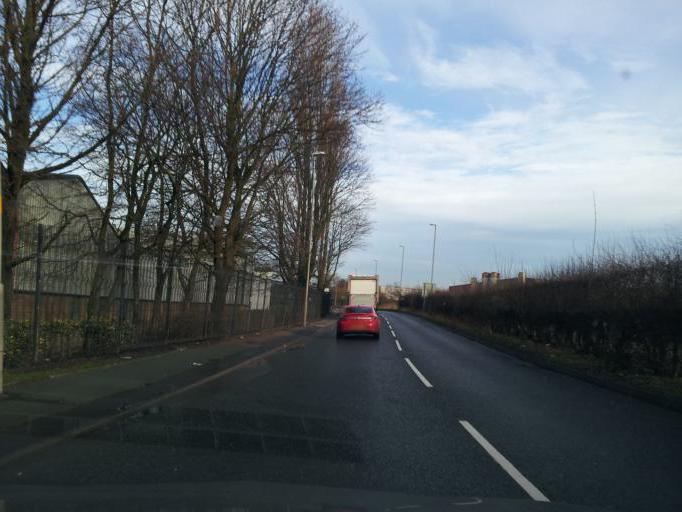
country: GB
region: England
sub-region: Manchester
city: Heywood
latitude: 53.5819
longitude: -2.2371
